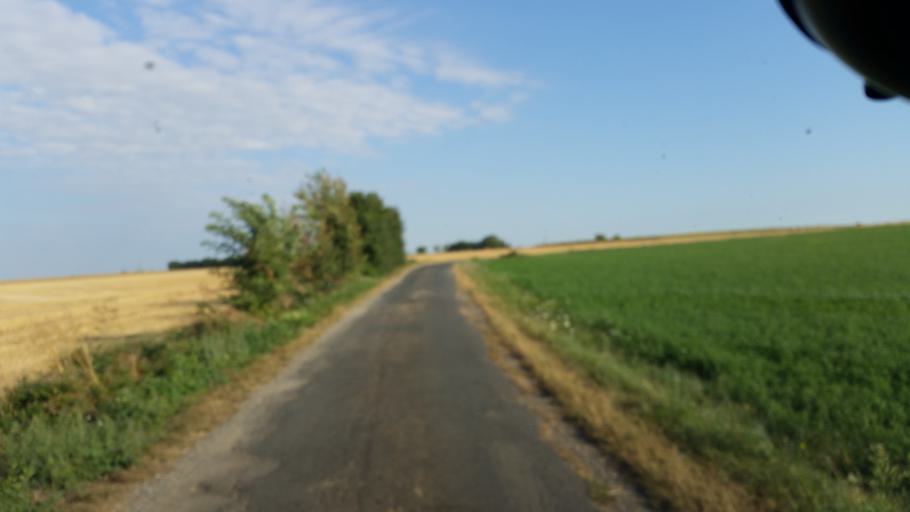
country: FR
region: Poitou-Charentes
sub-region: Departement de la Charente-Maritime
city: Saint-Jean-de-Liversay
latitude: 46.2317
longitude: -0.8896
